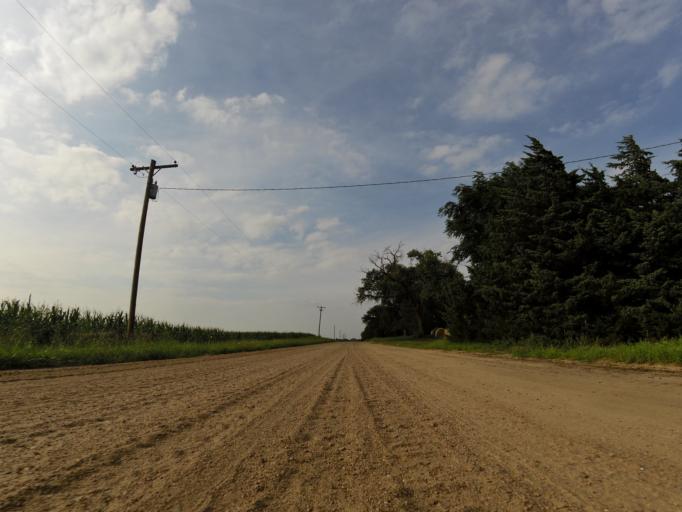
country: US
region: Kansas
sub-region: Reno County
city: South Hutchinson
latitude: 37.9730
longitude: -98.0688
